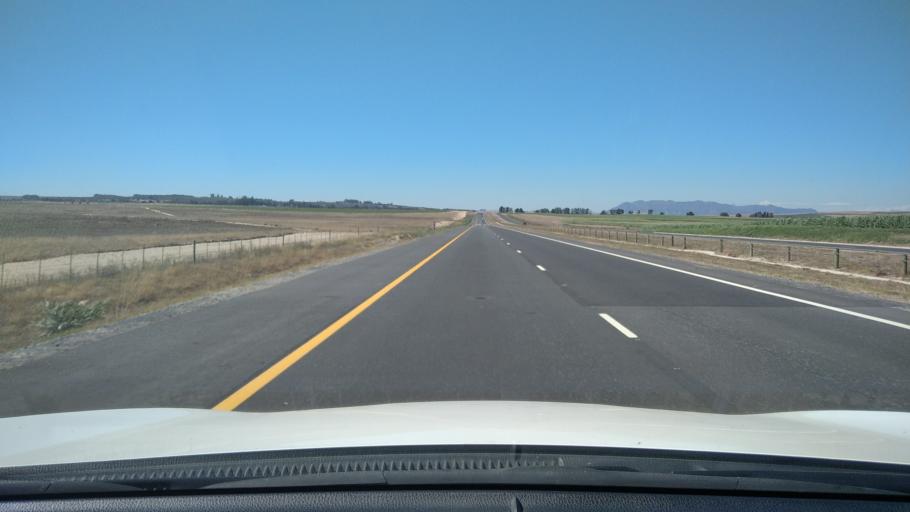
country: ZA
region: Western Cape
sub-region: West Coast District Municipality
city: Malmesbury
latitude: -33.5476
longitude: 18.6341
